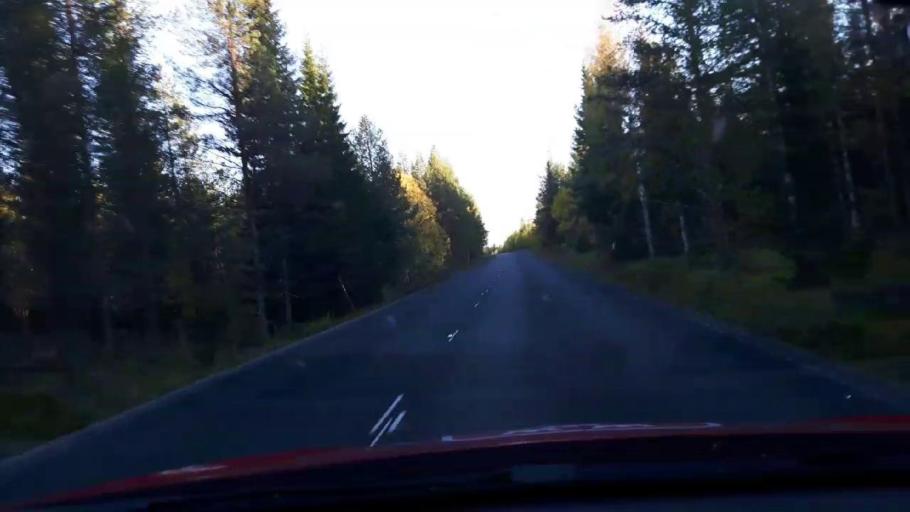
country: SE
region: Jaemtland
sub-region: OEstersunds Kommun
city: Lit
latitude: 63.4122
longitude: 14.8767
